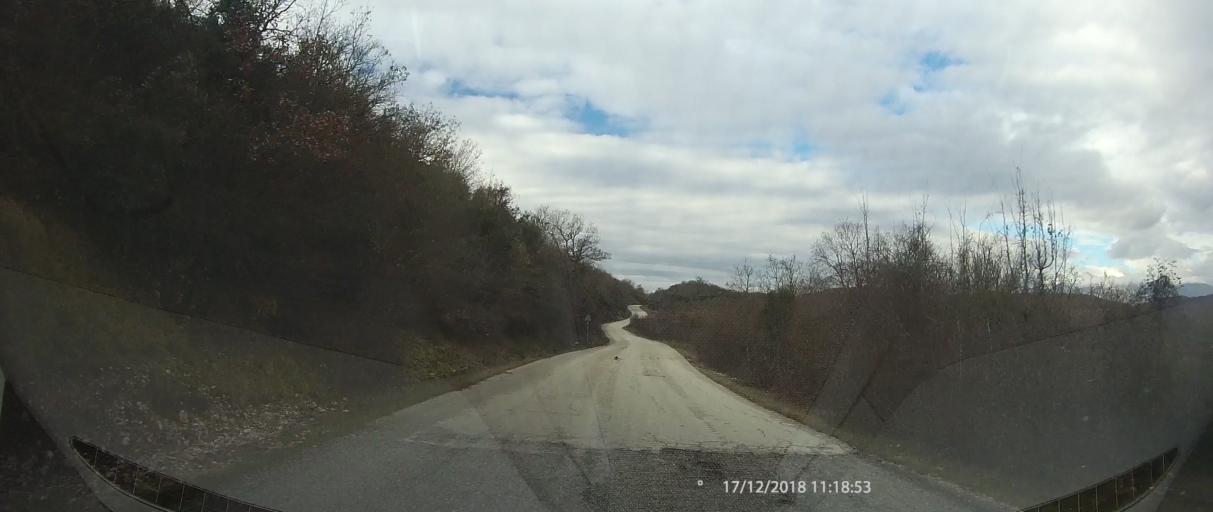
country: GR
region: Epirus
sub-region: Nomos Ioanninon
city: Kalpaki
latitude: 39.9563
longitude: 20.6546
